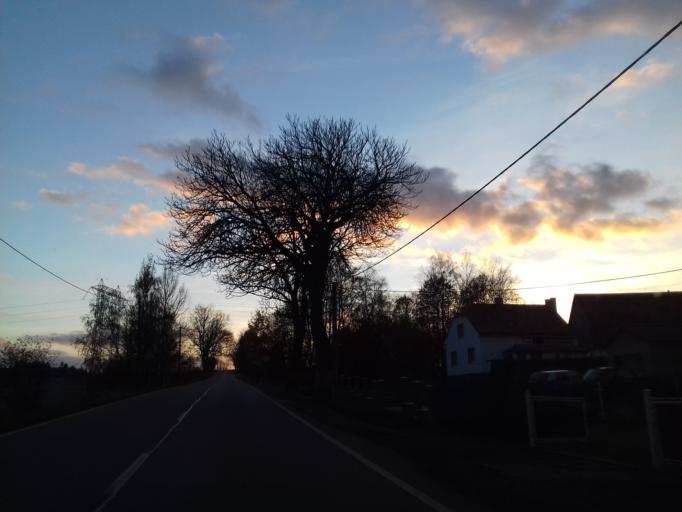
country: CZ
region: Vysocina
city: Krizova
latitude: 49.7161
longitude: 15.8567
